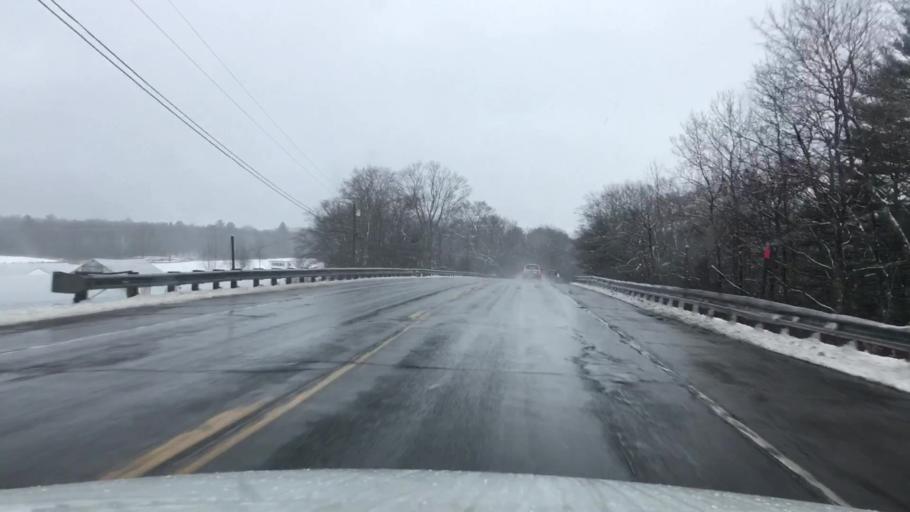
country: US
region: Maine
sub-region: Knox County
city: Warren
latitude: 44.1323
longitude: -69.2264
